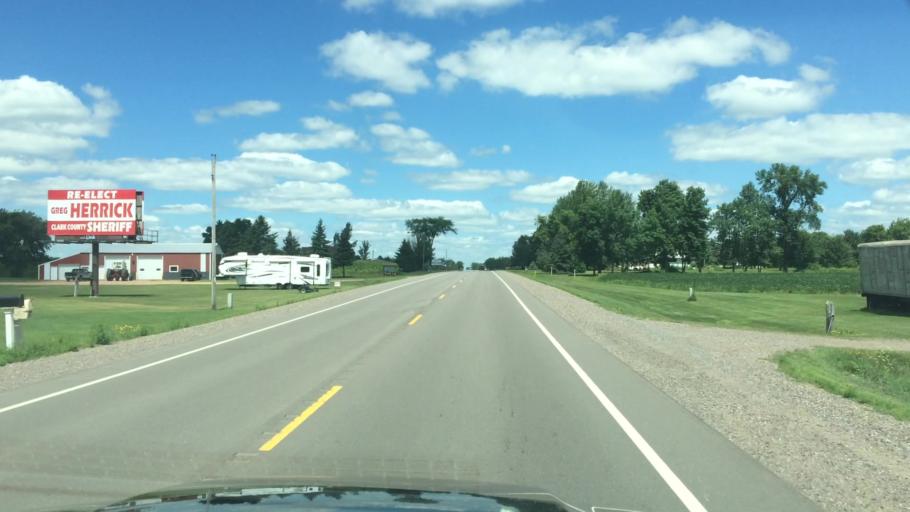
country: US
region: Wisconsin
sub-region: Clark County
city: Abbotsford
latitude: 45.0094
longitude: -90.3154
